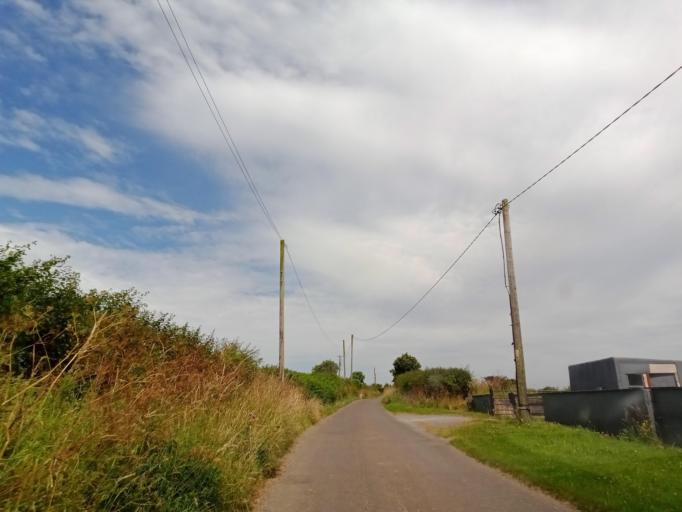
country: IE
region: Leinster
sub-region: Kilkenny
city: Thomastown
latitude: 52.5707
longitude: -7.1259
